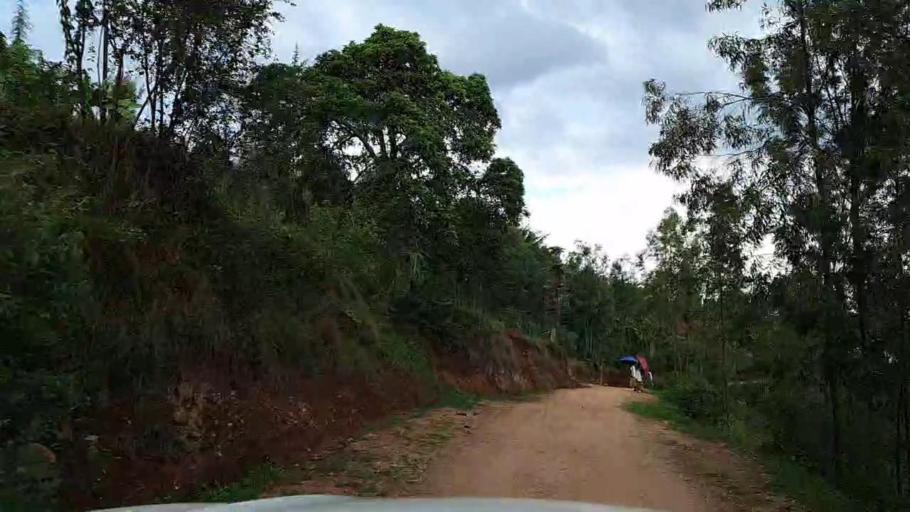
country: RW
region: Southern Province
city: Gikongoro
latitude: -2.4356
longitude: 29.6356
